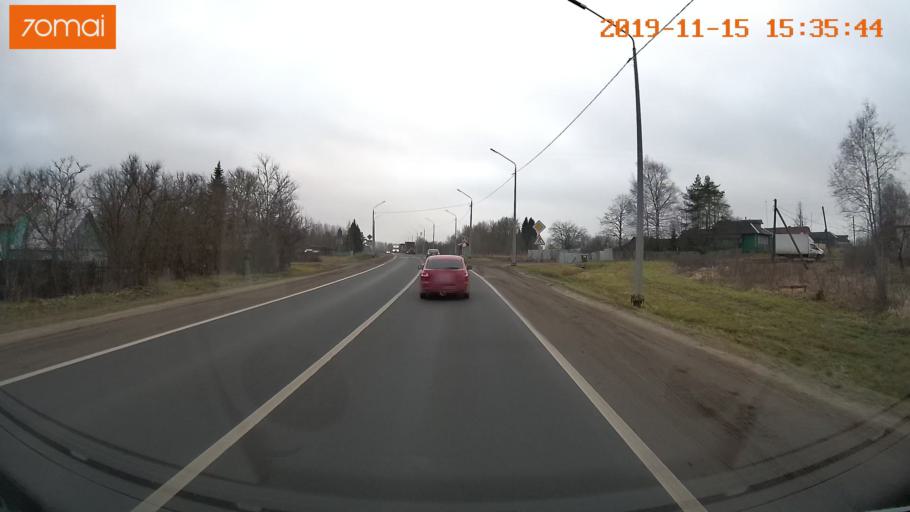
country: RU
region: Jaroslavl
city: Danilov
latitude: 58.0559
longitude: 40.0879
